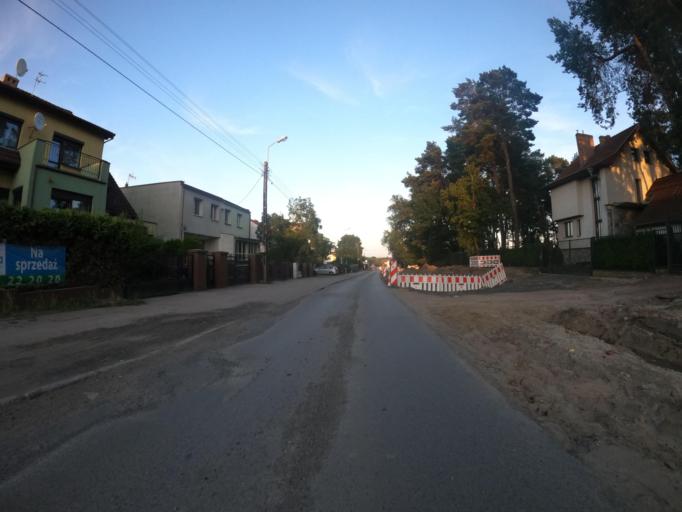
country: PL
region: West Pomeranian Voivodeship
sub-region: Powiat policki
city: Przeclaw
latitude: 53.4559
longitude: 14.4671
